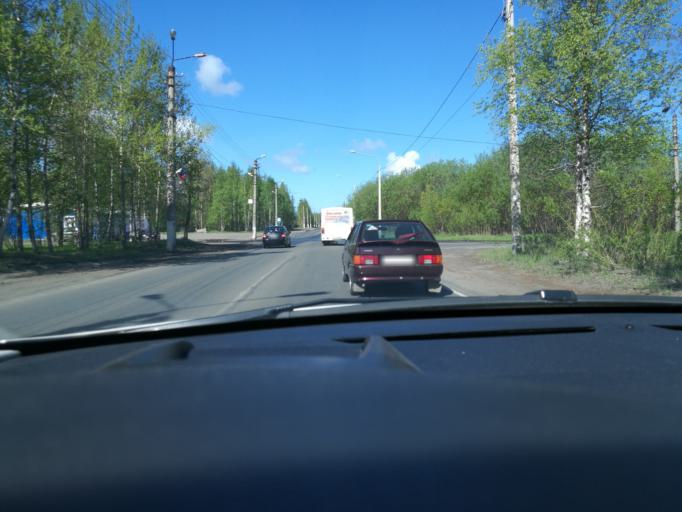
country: RU
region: Arkhangelskaya
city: Arkhangel'sk
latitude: 64.5966
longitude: 40.5663
